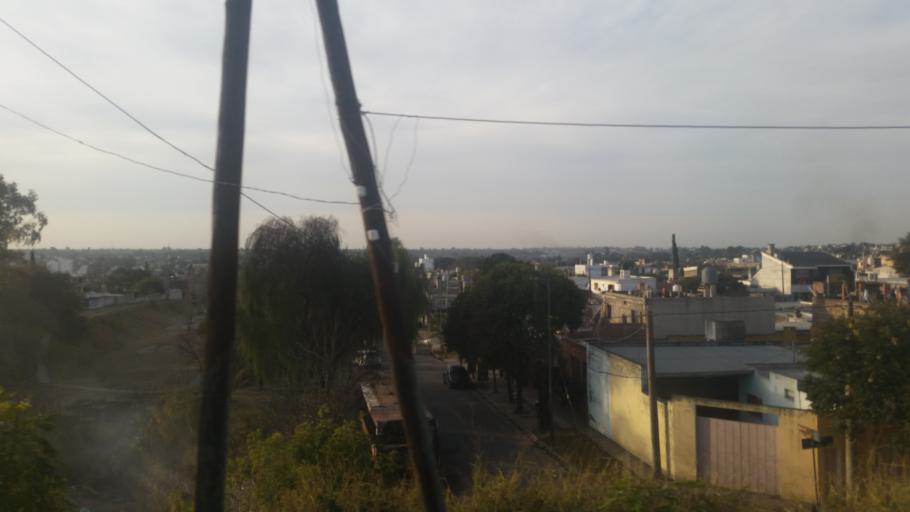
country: AR
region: Cordoba
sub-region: Departamento de Capital
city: Cordoba
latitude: -31.4315
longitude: -64.1456
